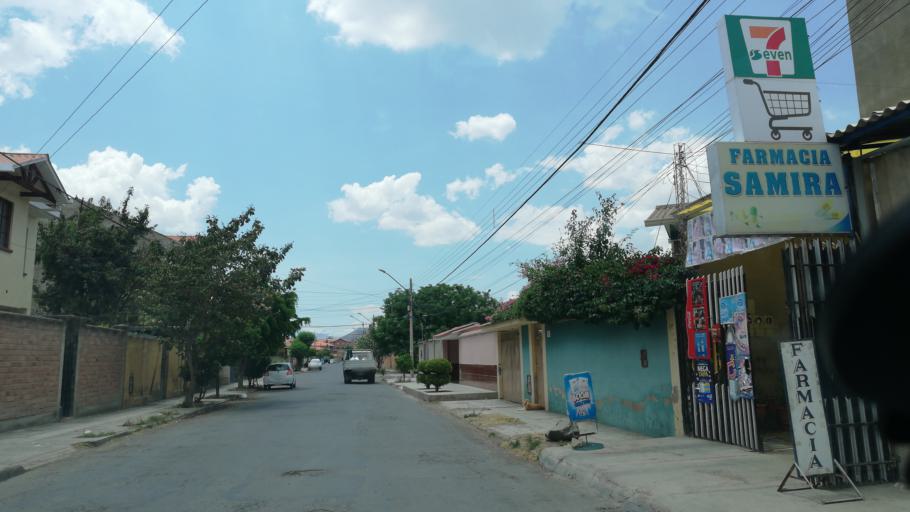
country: BO
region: Cochabamba
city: Cochabamba
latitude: -17.3780
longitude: -66.1941
